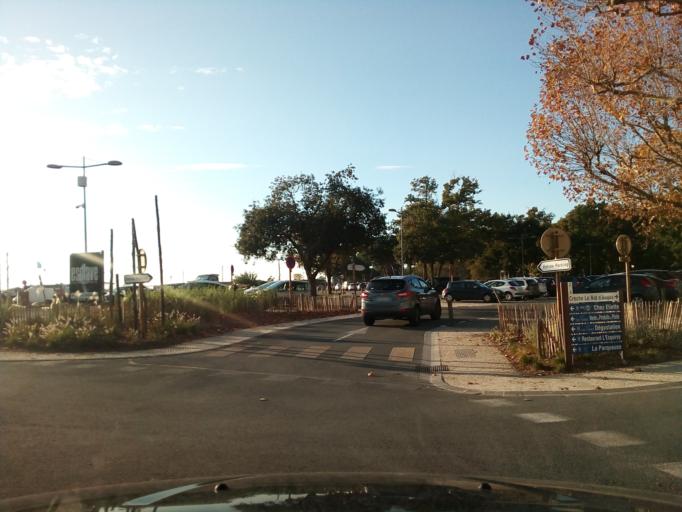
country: FR
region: Aquitaine
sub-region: Departement de la Gironde
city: Andernos-les-Bains
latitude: 44.7437
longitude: -1.1061
